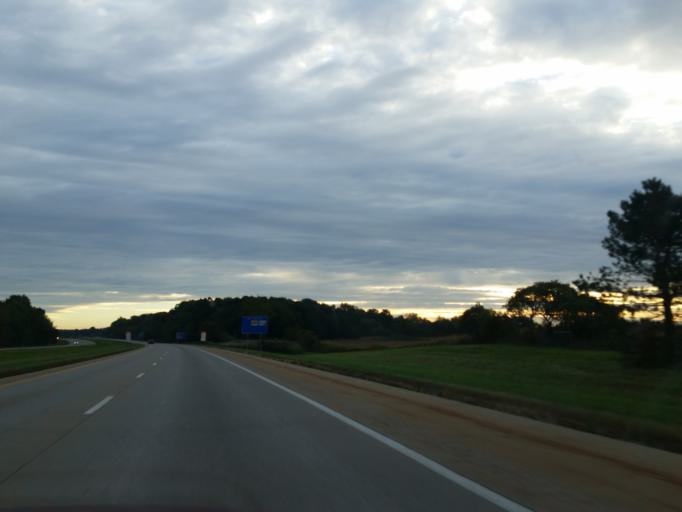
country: US
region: Ohio
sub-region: Ashtabula County
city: Geneva
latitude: 41.7732
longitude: -80.8823
